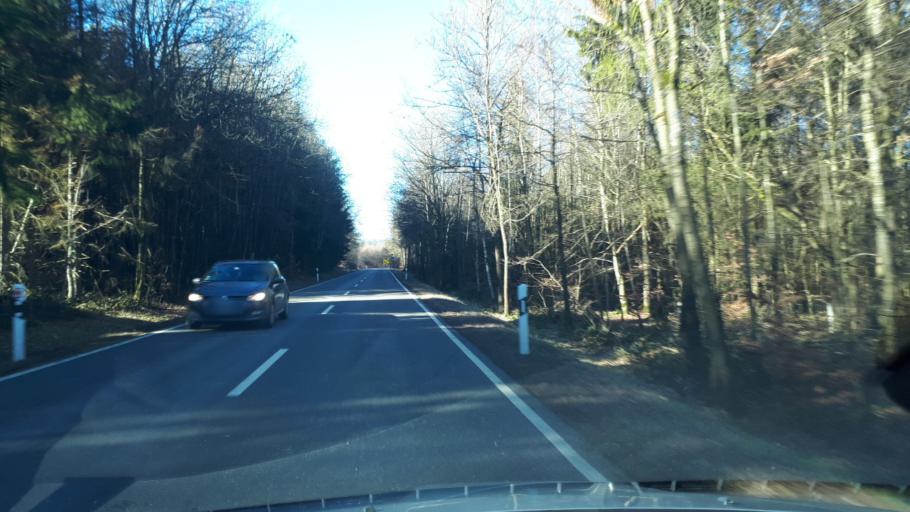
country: DE
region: Rheinland-Pfalz
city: Ellscheid
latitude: 50.1580
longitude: 6.9232
